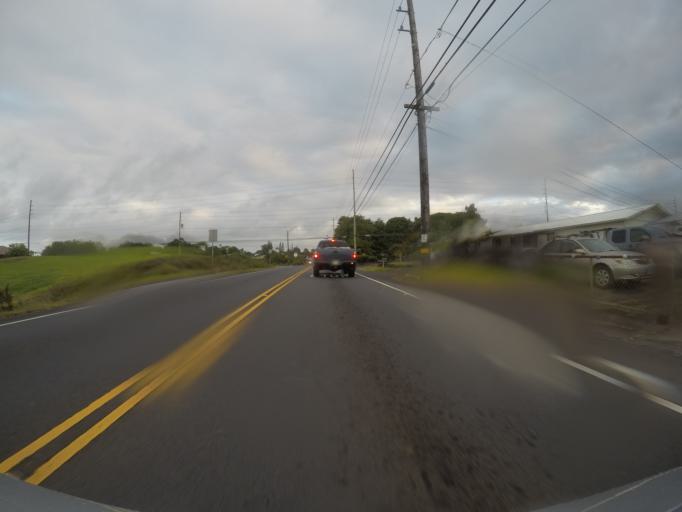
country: US
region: Hawaii
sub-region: Hawaii County
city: Hilo
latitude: 19.6839
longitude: -155.0898
